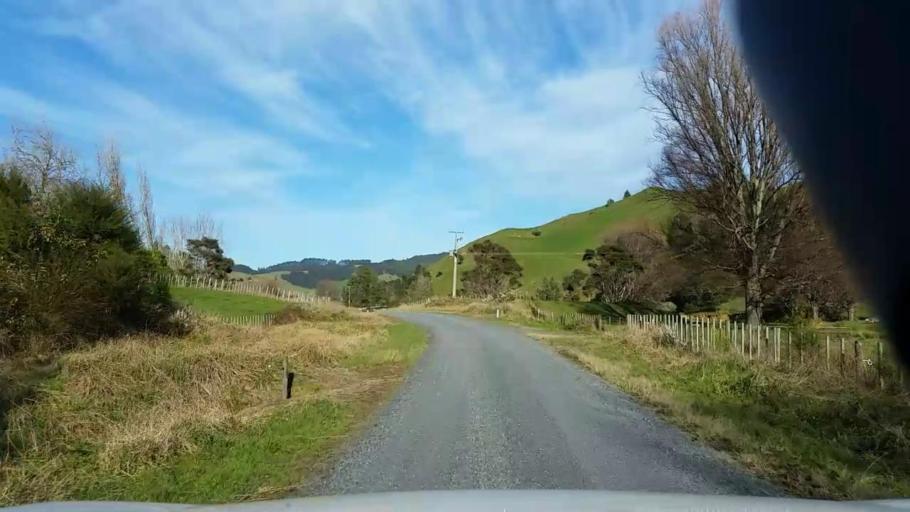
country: NZ
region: Waikato
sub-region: Hauraki District
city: Ngatea
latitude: -37.4526
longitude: 175.4067
